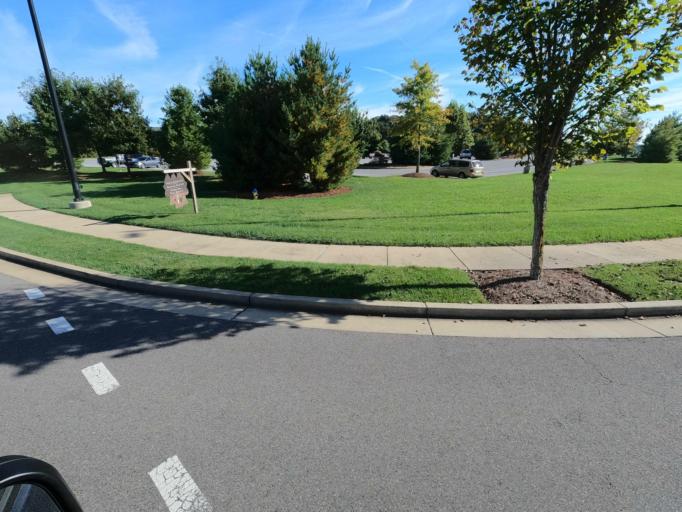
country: US
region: Tennessee
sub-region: Sullivan County
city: Walnut Hill
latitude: 36.5952
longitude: -82.2533
